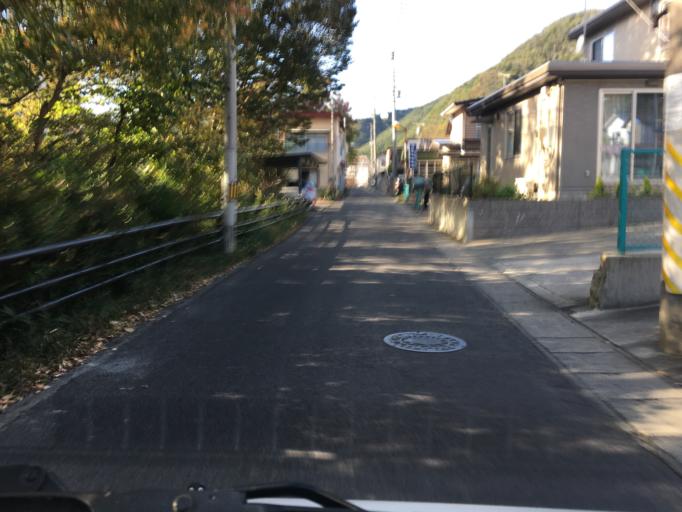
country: JP
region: Fukushima
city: Fukushima-shi
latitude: 37.8350
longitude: 140.4533
